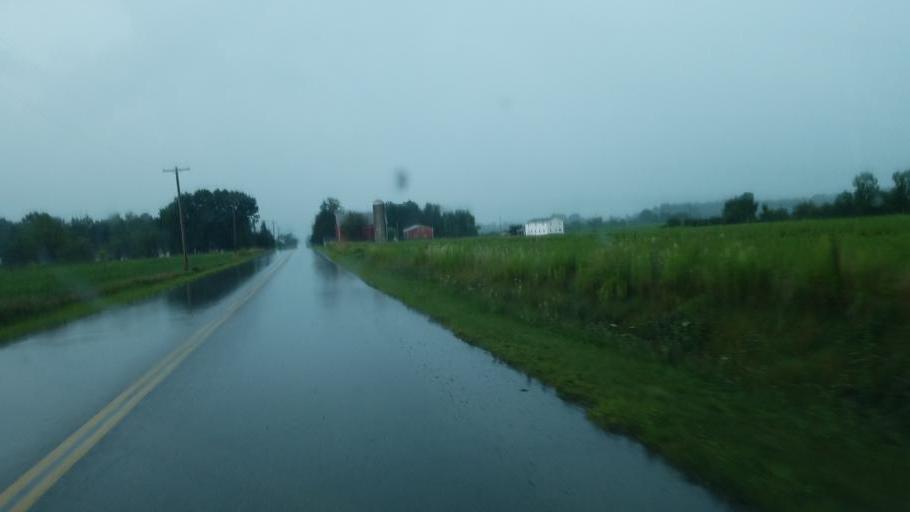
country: US
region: Ohio
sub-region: Geauga County
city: Middlefield
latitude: 41.5087
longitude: -80.9769
